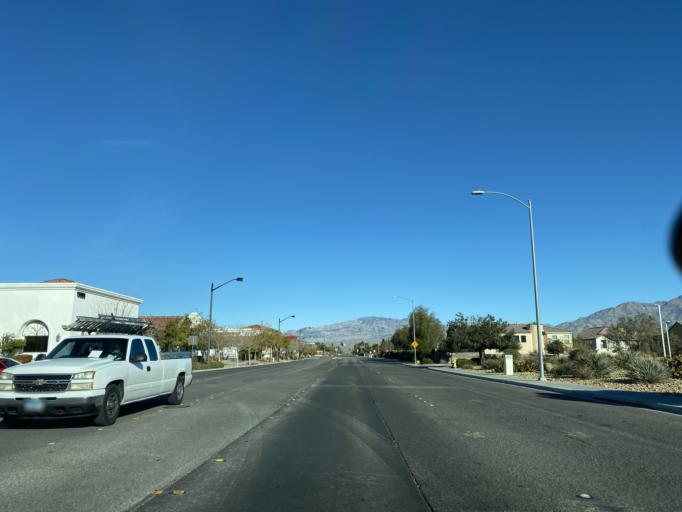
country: US
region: Nevada
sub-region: Clark County
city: Las Vegas
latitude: 36.2964
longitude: -115.2786
